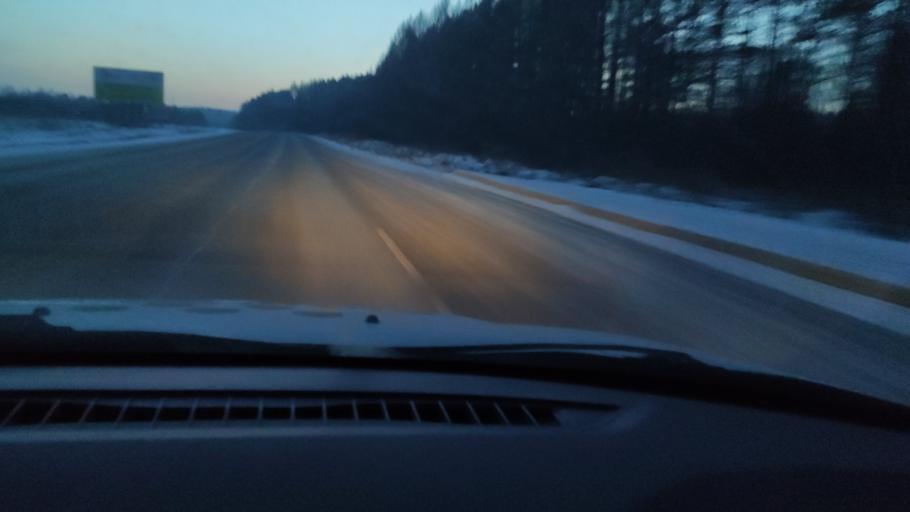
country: RU
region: Perm
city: Kungur
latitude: 57.4199
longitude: 56.9200
